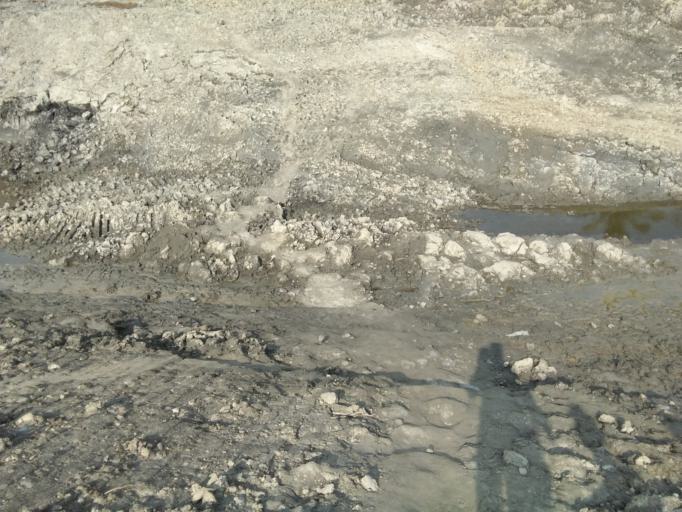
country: IN
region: West Bengal
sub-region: North 24 Parganas
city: Taki
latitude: 22.5915
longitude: 89.0339
